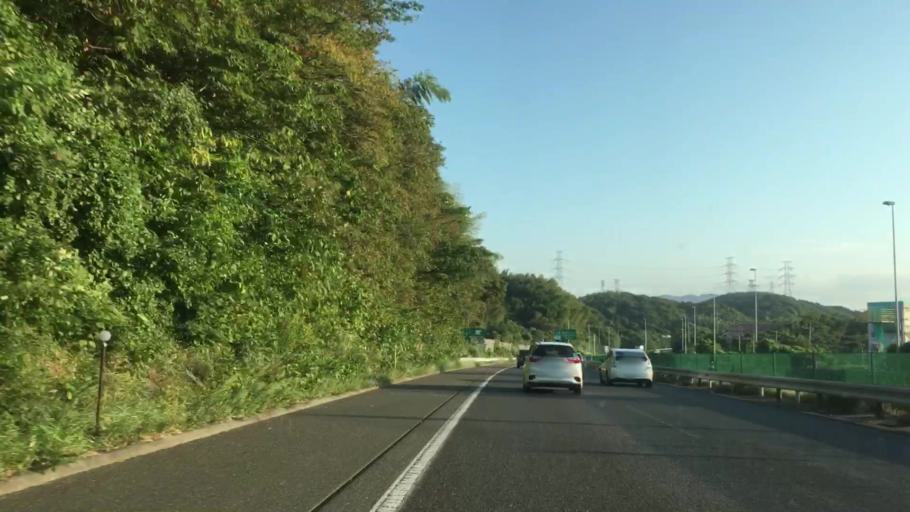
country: JP
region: Yamaguchi
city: Shimonoseki
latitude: 33.9829
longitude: 130.9521
